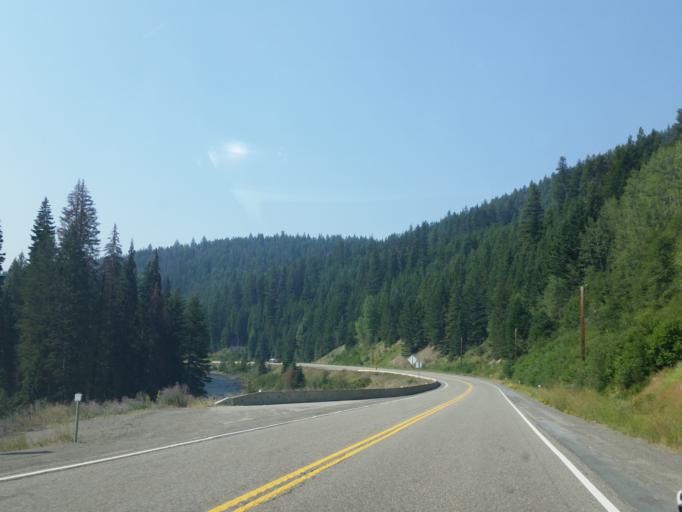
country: CA
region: British Columbia
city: Princeton
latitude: 49.1658
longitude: -120.5796
